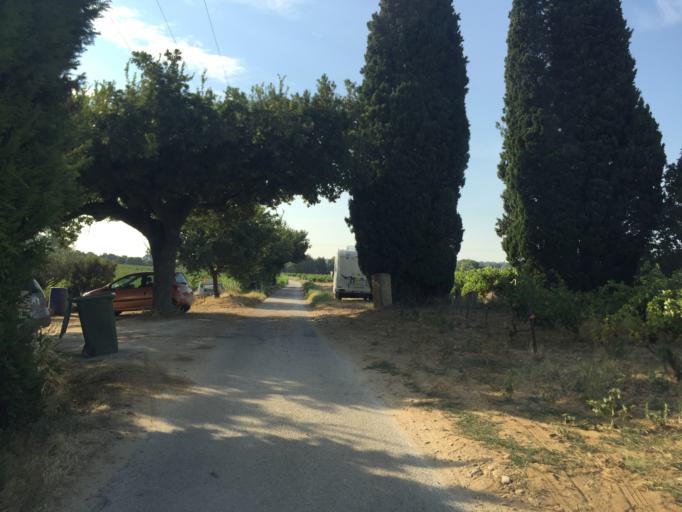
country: FR
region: Provence-Alpes-Cote d'Azur
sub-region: Departement du Vaucluse
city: Courthezon
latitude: 44.0834
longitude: 4.8592
